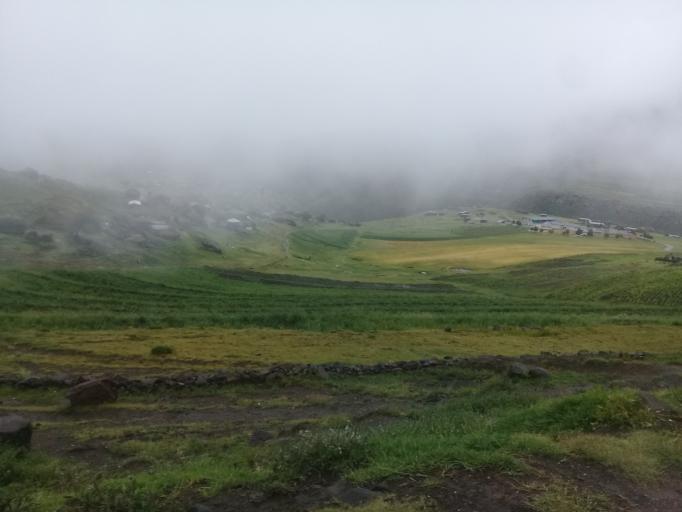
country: LS
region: Mokhotlong
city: Mokhotlong
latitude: -29.3769
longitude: 28.9867
